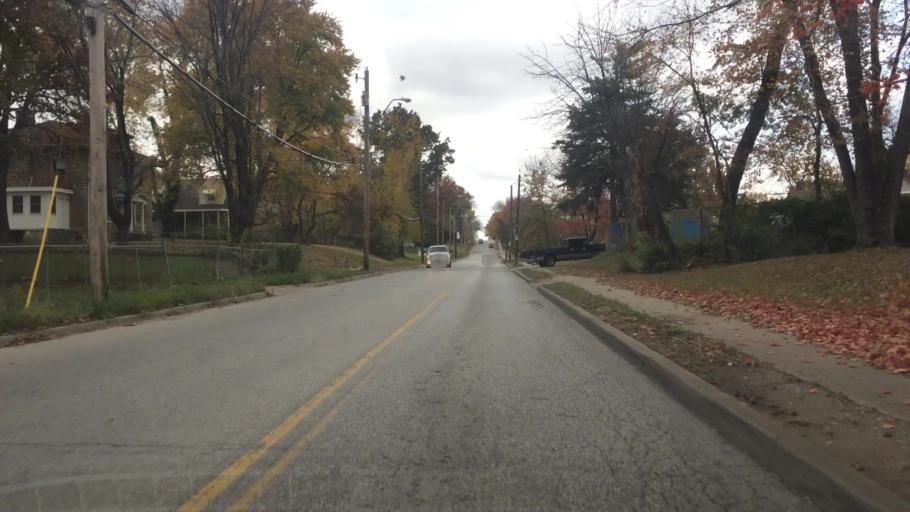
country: US
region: Kansas
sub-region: Johnson County
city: Leawood
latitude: 38.9922
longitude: -94.5432
